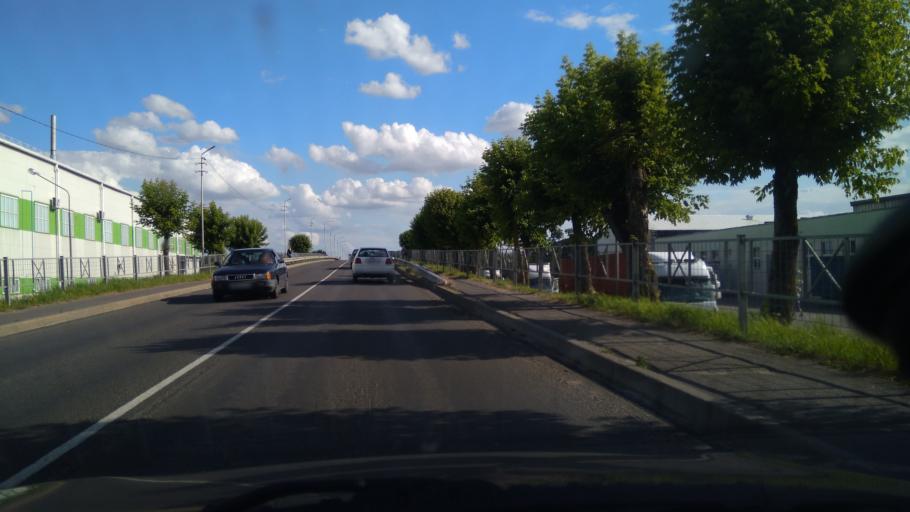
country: BY
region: Grodnenskaya
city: Masty
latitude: 53.4057
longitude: 24.5355
